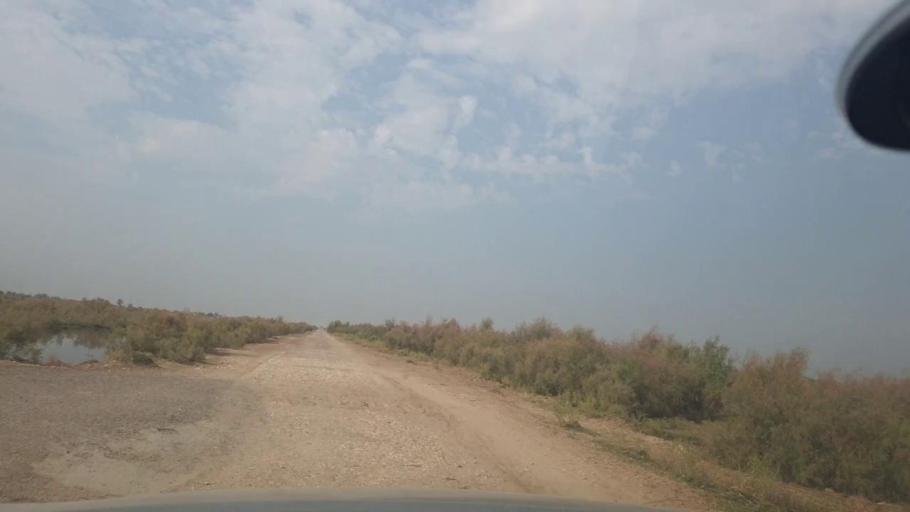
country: PK
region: Balochistan
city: Mehrabpur
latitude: 28.0295
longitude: 68.1484
